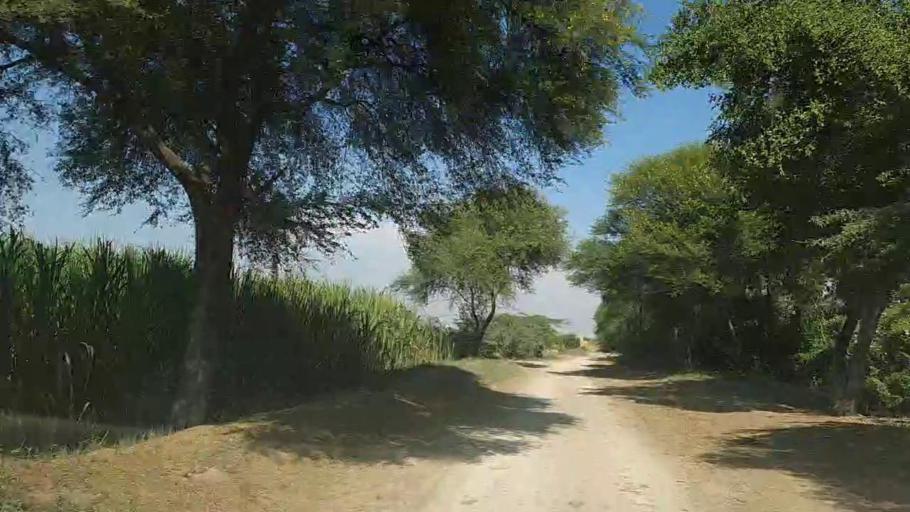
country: PK
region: Sindh
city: Mirpur Batoro
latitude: 24.7549
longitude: 68.2890
